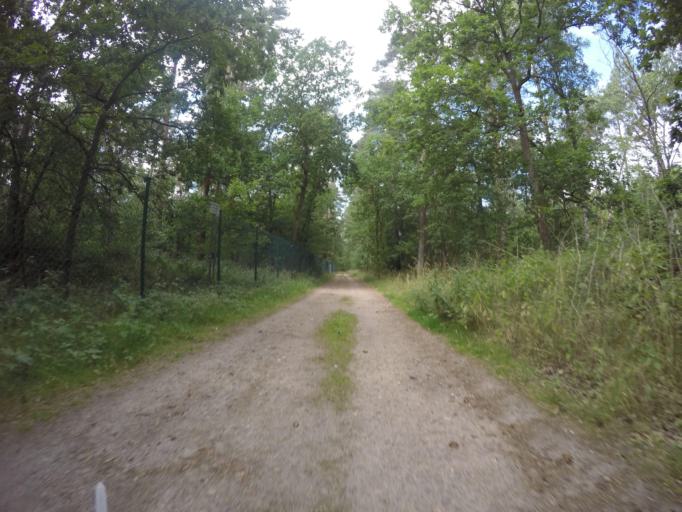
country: DE
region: Lower Saxony
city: Bleckede
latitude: 53.2775
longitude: 10.7287
